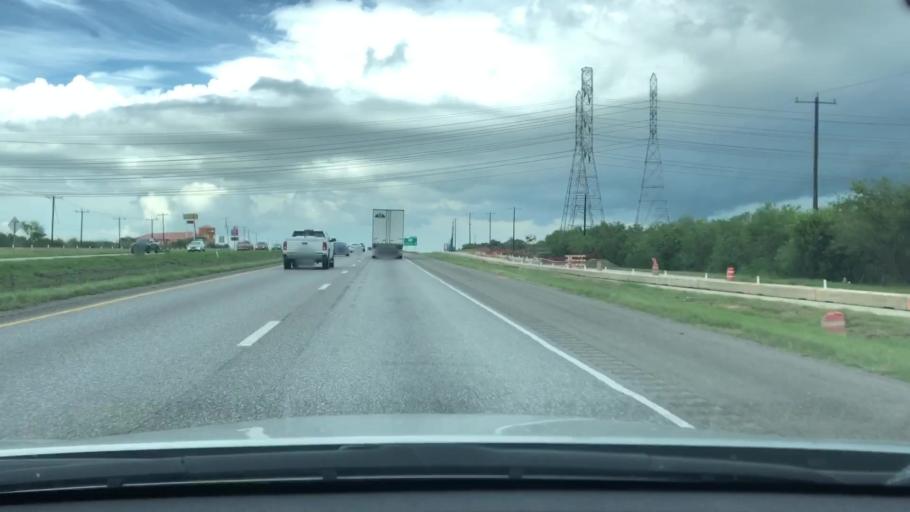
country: US
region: Texas
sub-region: Bexar County
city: Kirby
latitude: 29.4558
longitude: -98.3251
